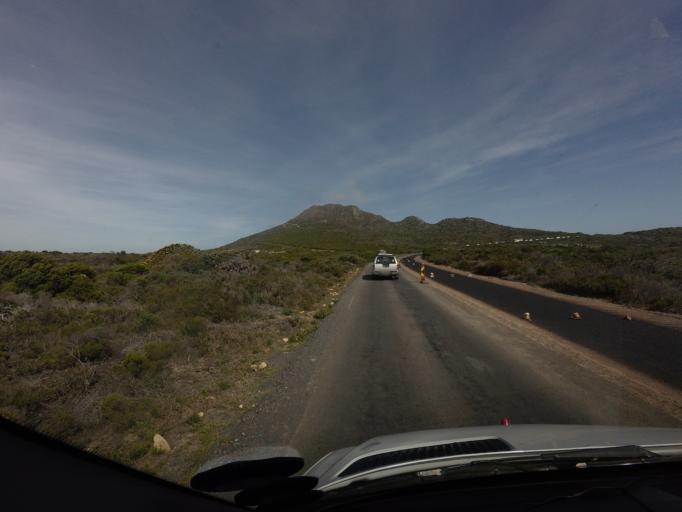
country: ZA
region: Western Cape
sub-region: City of Cape Town
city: Retreat
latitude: -34.3375
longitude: 18.4650
